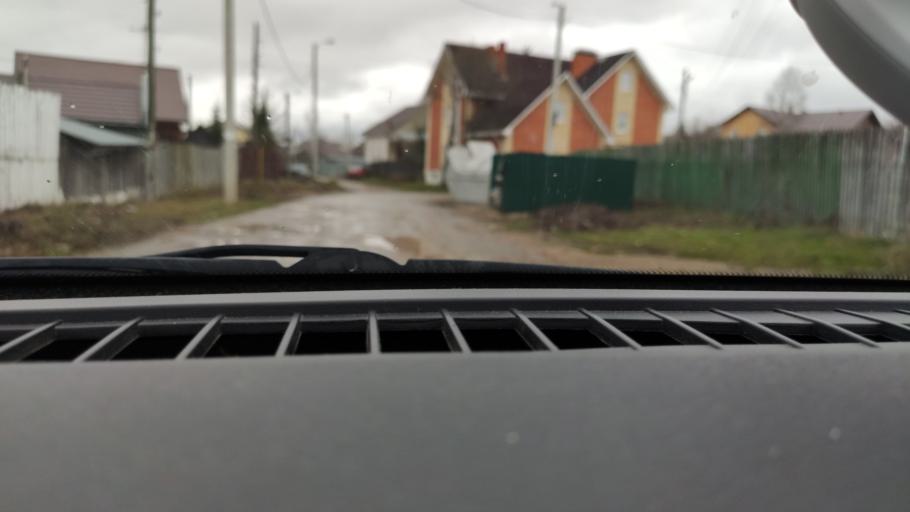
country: RU
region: Perm
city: Froly
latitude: 57.9468
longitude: 56.3050
